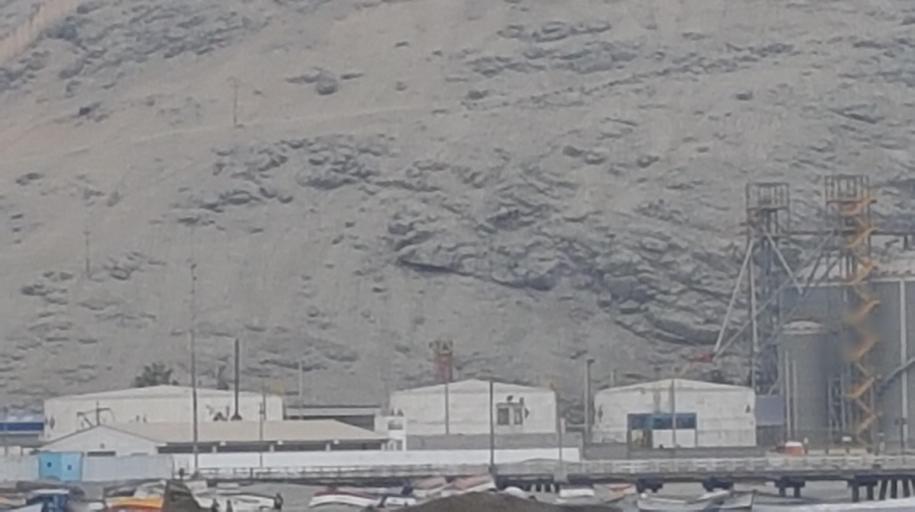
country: PE
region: La Libertad
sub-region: Provincia de Trujillo
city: Salaverry
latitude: -8.2208
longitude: -78.9833
